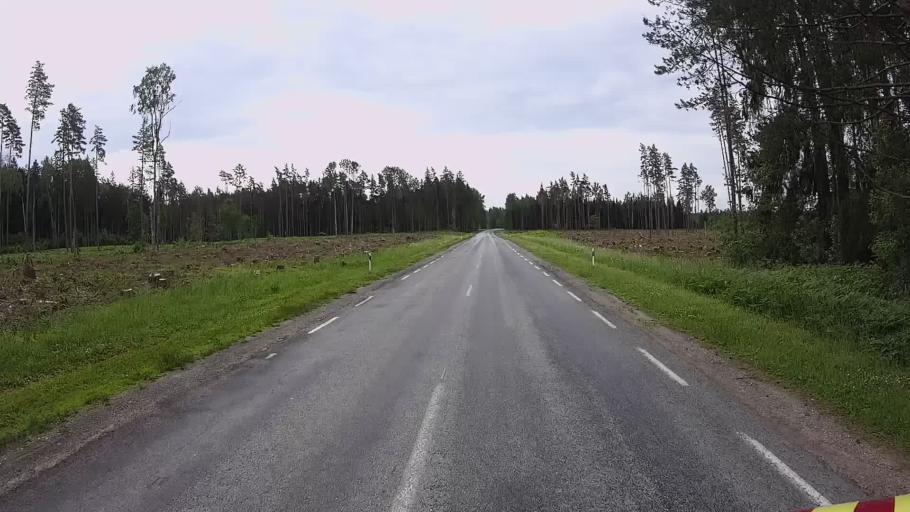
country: EE
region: Viljandimaa
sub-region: Karksi vald
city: Karksi-Nuia
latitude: 58.2222
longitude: 25.6155
